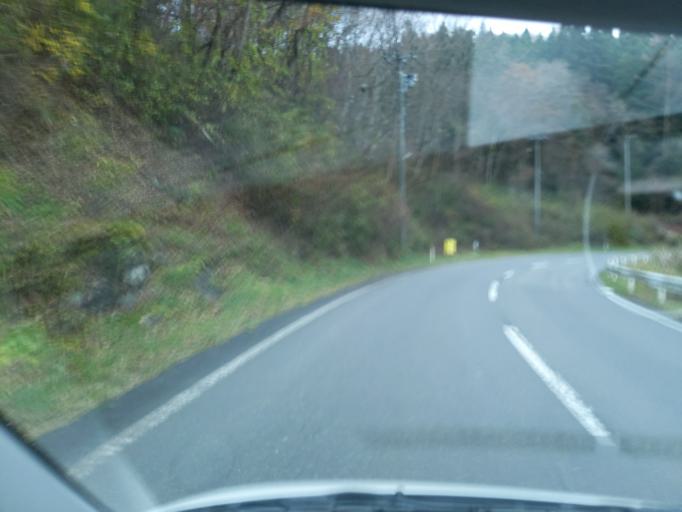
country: JP
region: Iwate
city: Mizusawa
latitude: 39.0365
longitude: 141.3427
